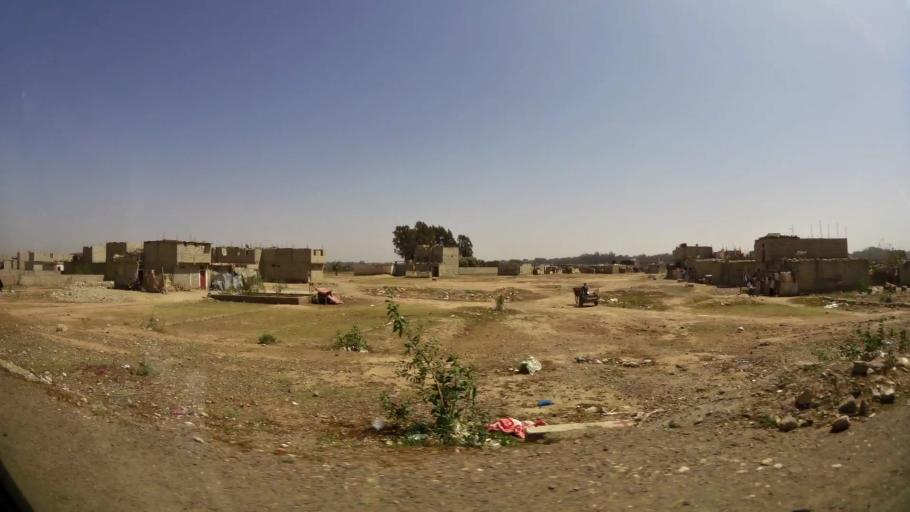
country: MA
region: Souss-Massa-Draa
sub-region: Inezgane-Ait Mellou
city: Inezgane
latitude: 30.3440
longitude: -9.5516
